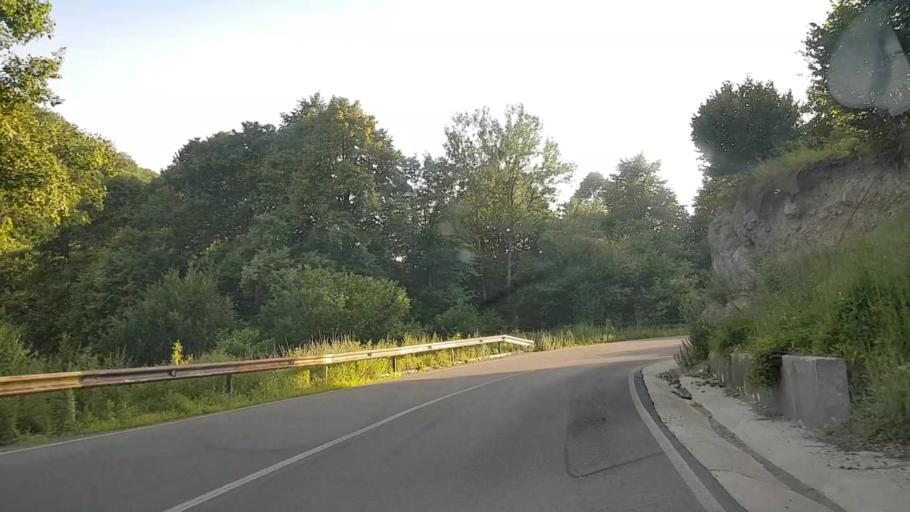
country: RO
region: Harghita
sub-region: Comuna Praid
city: Ocna de Sus
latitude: 46.5718
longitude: 25.2001
